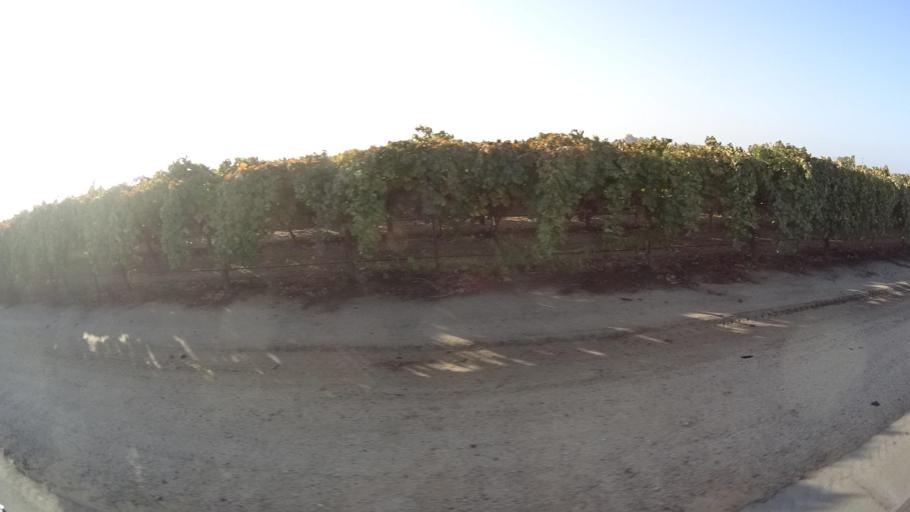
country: US
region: California
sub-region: Kern County
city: Delano
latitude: 35.7905
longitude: -119.1844
